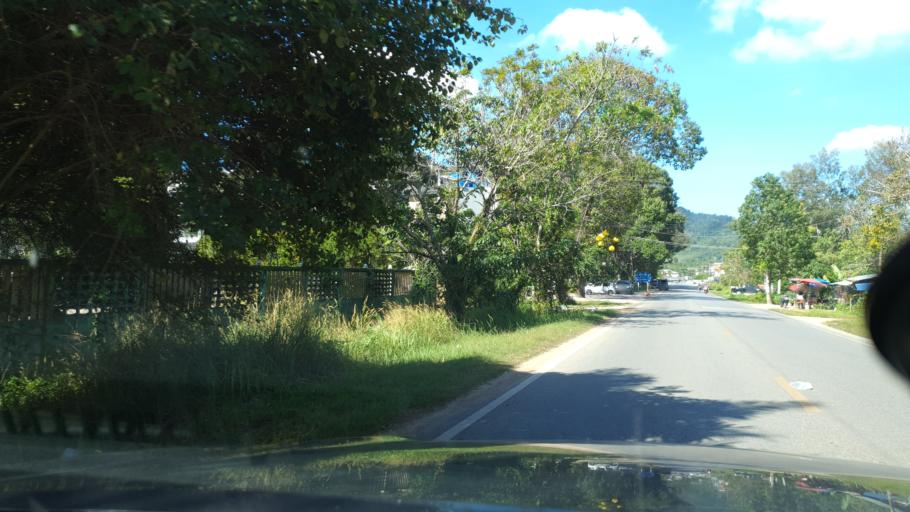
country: TH
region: Phangnga
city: Ban Ao Nang
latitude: 8.0294
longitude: 98.8679
